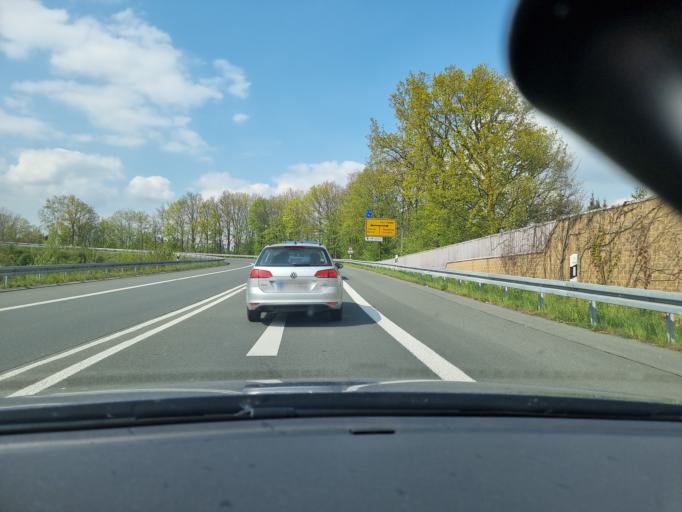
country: DE
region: North Rhine-Westphalia
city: Buende
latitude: 52.1950
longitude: 8.5492
